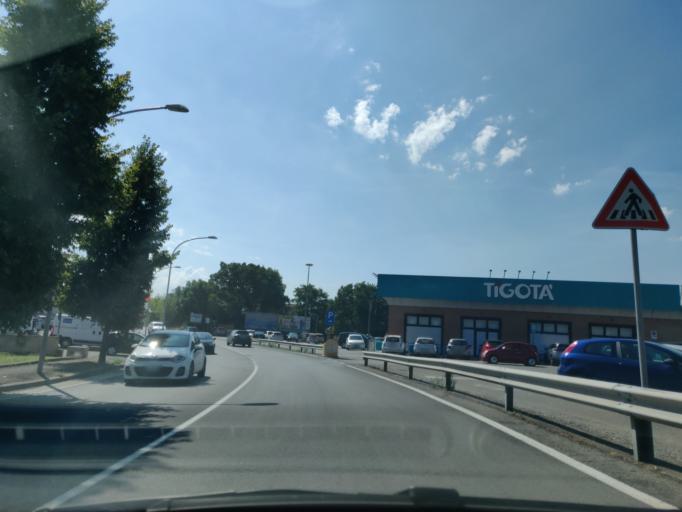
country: IT
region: Latium
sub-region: Provincia di Viterbo
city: Viterbo
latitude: 42.4238
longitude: 12.0934
